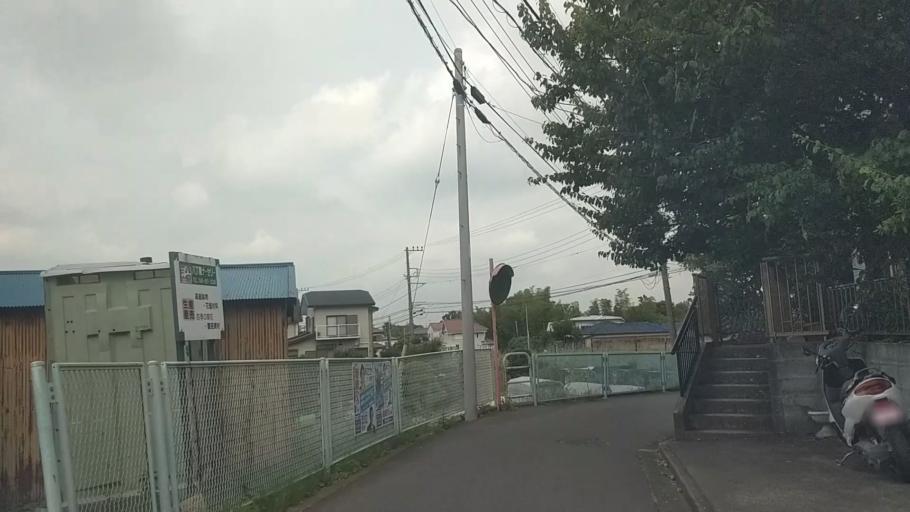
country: JP
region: Kanagawa
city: Fujisawa
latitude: 35.3837
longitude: 139.5097
